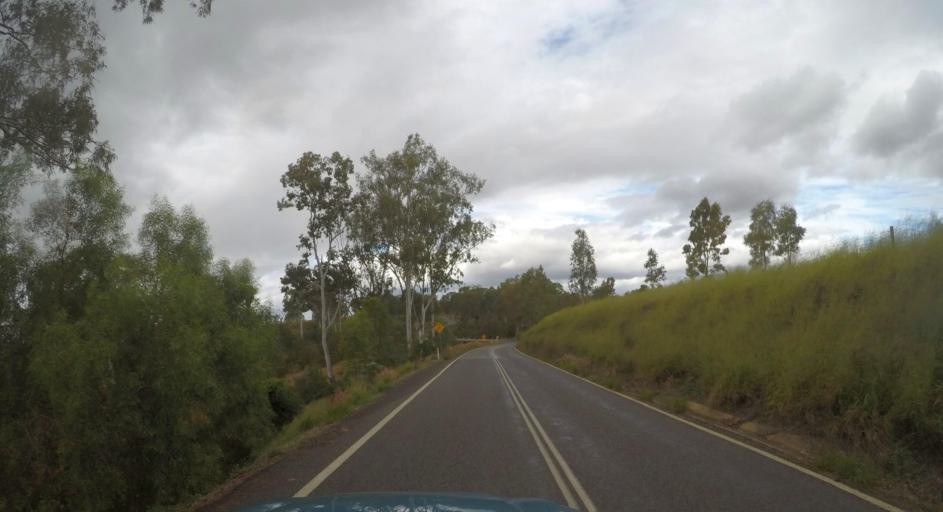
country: AU
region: Queensland
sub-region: North Burnett
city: Gayndah
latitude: -25.6707
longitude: 151.2425
